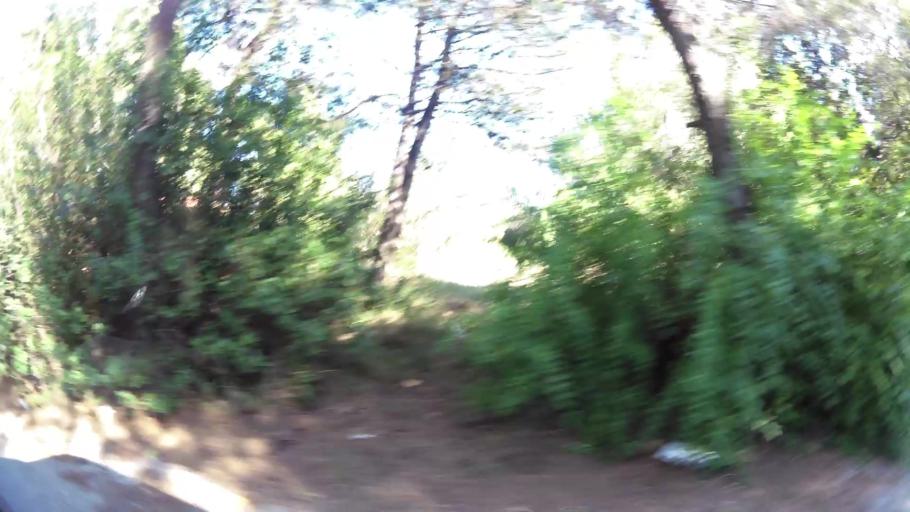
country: GR
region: Attica
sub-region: Nomarchia Athinas
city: Ekali
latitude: 38.1170
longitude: 23.8451
